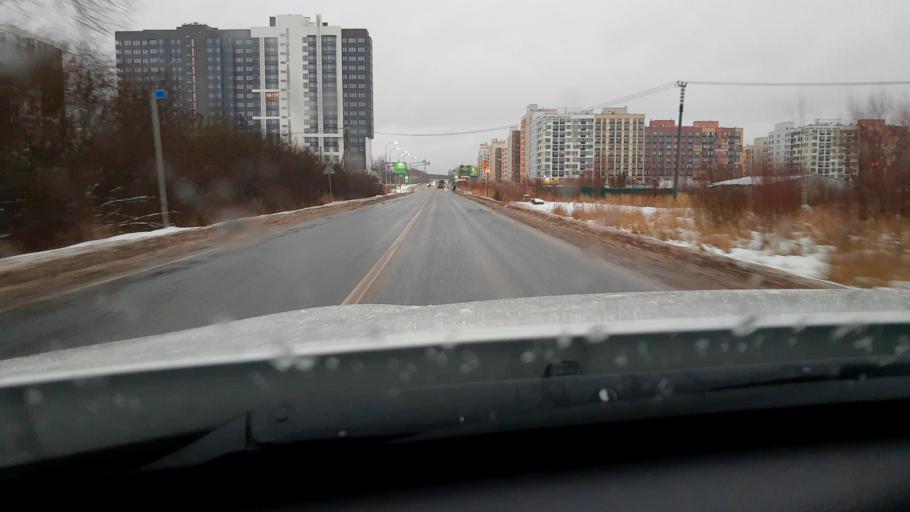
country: RU
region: Moskovskaya
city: Krasnogorsk
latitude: 55.8689
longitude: 37.3170
